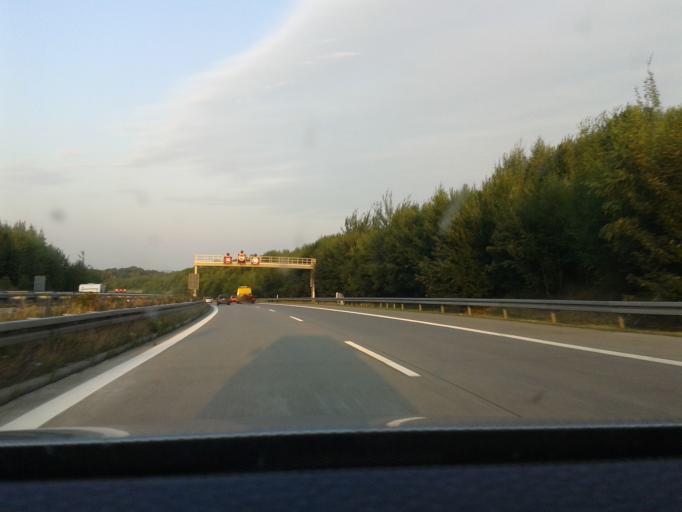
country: DE
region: Saxony
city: Freital
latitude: 51.0351
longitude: 13.6355
